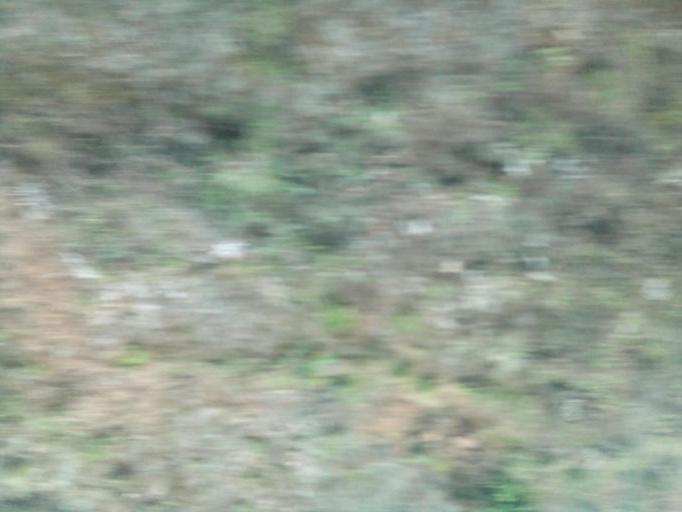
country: BR
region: Minas Gerais
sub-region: Caete
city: Caete
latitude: -19.9133
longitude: -43.7003
